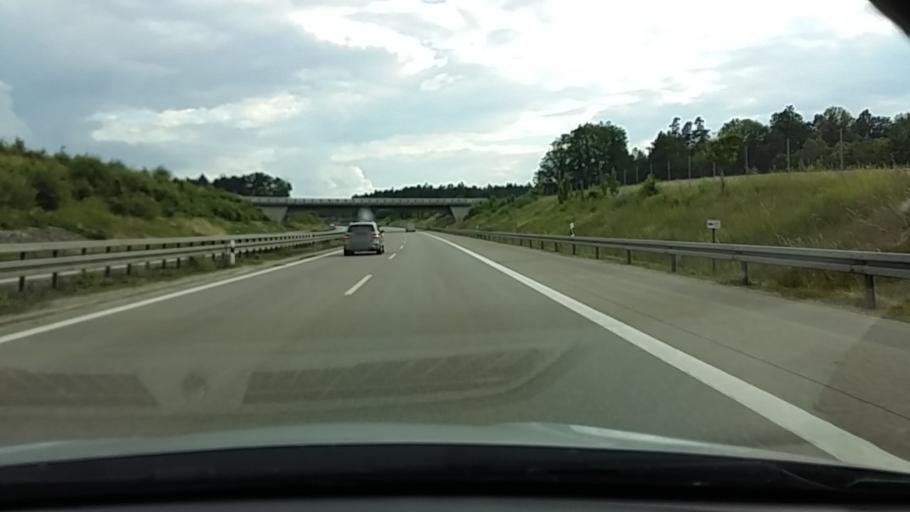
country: DE
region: Bavaria
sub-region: Upper Palatinate
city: Ebermannsdorf
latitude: 49.4236
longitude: 12.0016
